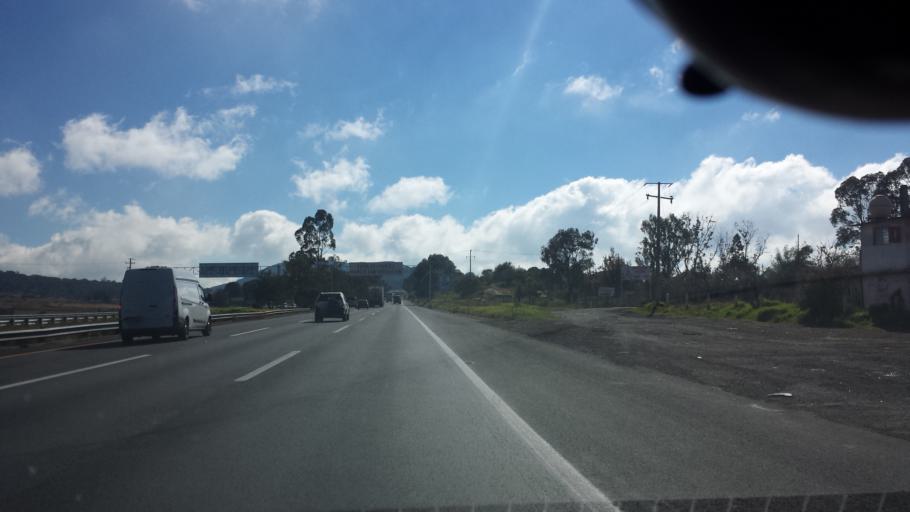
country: MX
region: Mexico
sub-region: Jilotepec
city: San Vicente (Calpulalpan Tercera Manzana)
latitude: 20.0825
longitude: -99.6609
